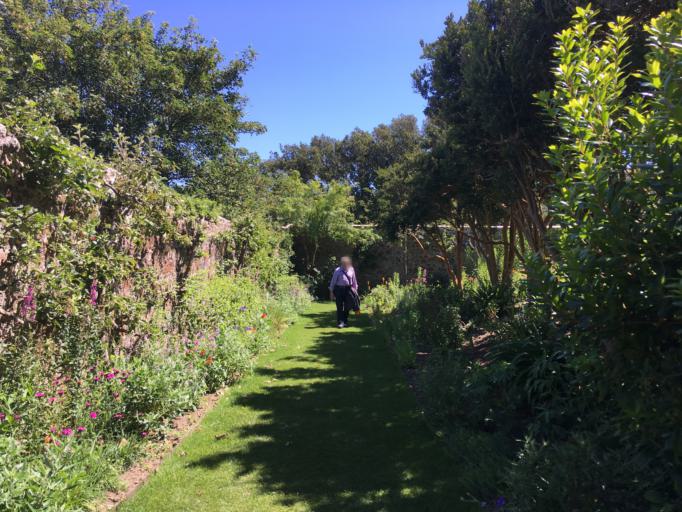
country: GG
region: St Peter Port
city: Saint Peter Port
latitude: 49.4509
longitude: -2.5371
